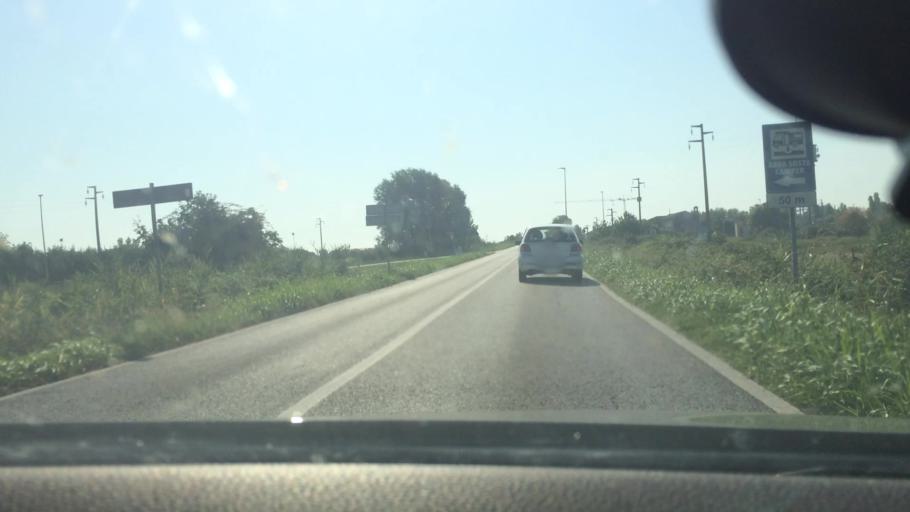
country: IT
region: Emilia-Romagna
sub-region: Provincia di Ferrara
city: Comacchio
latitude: 44.7025
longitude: 12.1676
